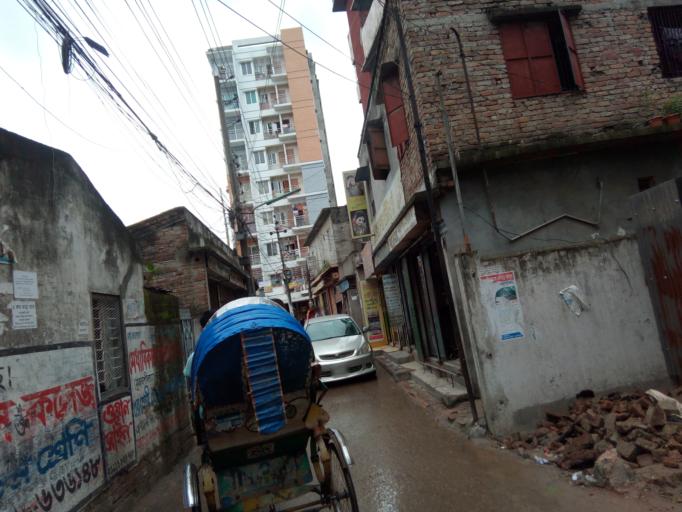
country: BD
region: Dhaka
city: Azimpur
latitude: 23.7493
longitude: 90.3641
